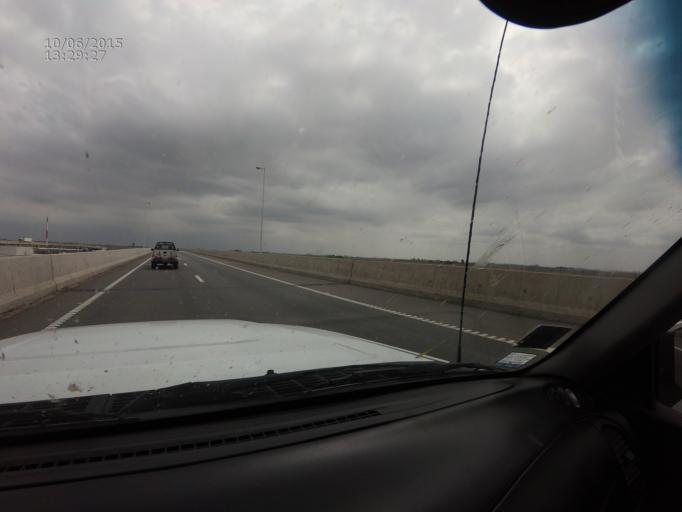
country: AR
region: Cordoba
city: Leones
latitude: -32.6380
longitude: -62.2445
